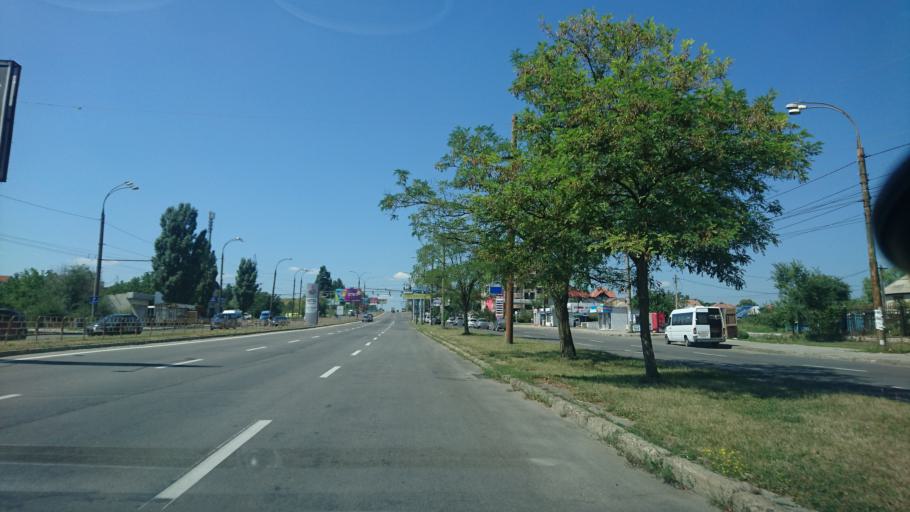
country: MD
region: Laloveni
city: Ialoveni
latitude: 46.9963
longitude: 28.8018
